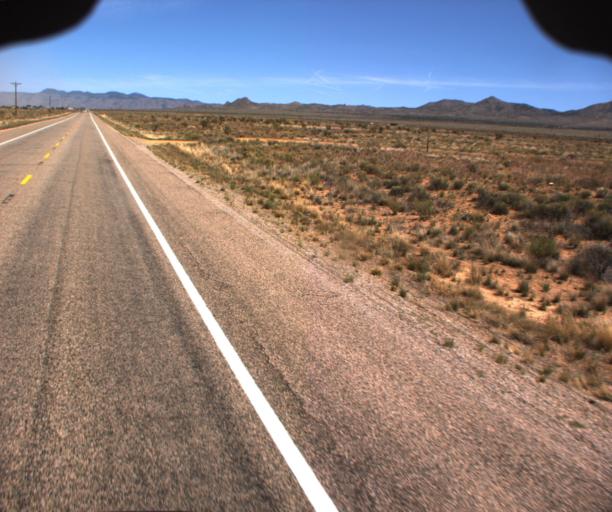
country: US
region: Arizona
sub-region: Mohave County
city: New Kingman-Butler
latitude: 35.3641
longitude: -113.8701
